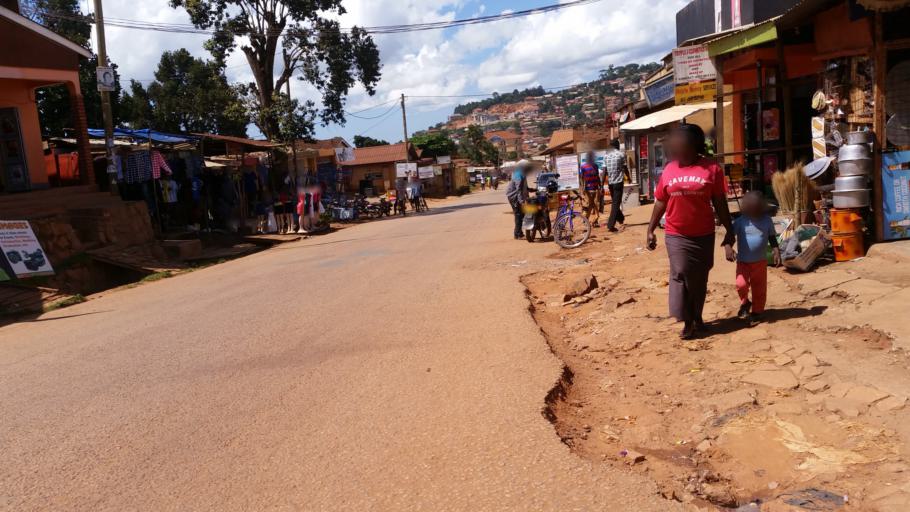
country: UG
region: Central Region
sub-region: Wakiso District
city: Kireka
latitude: 0.3495
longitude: 32.6461
